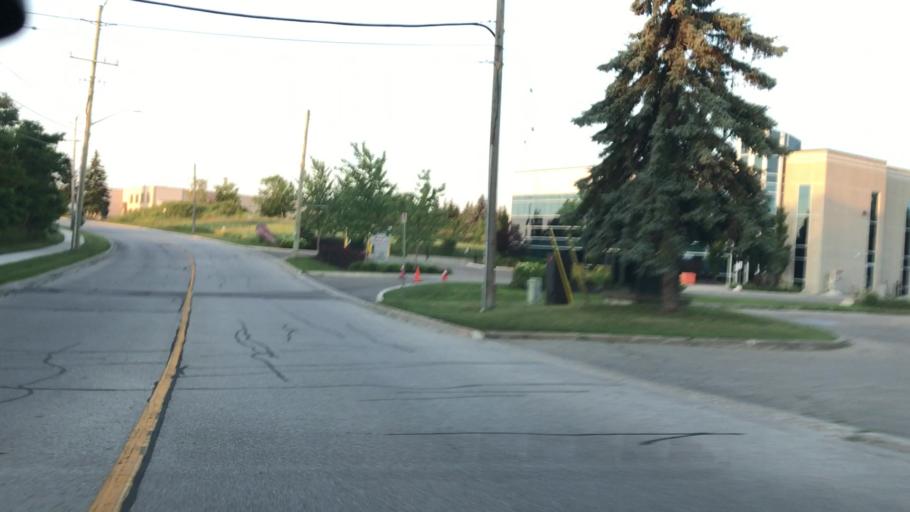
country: CA
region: Ontario
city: Newmarket
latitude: 44.0101
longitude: -79.4616
